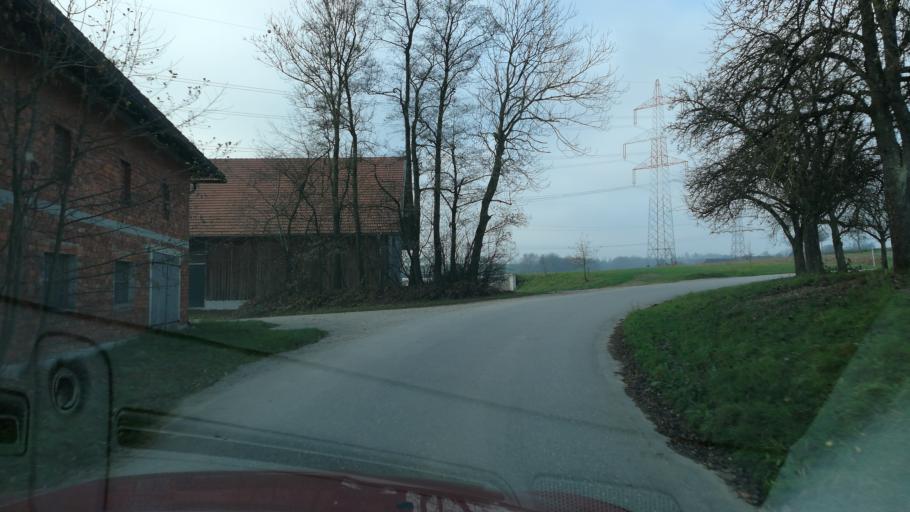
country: AT
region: Upper Austria
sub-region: Politischer Bezirk Kirchdorf an der Krems
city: Kremsmunster
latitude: 48.1010
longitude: 14.1787
